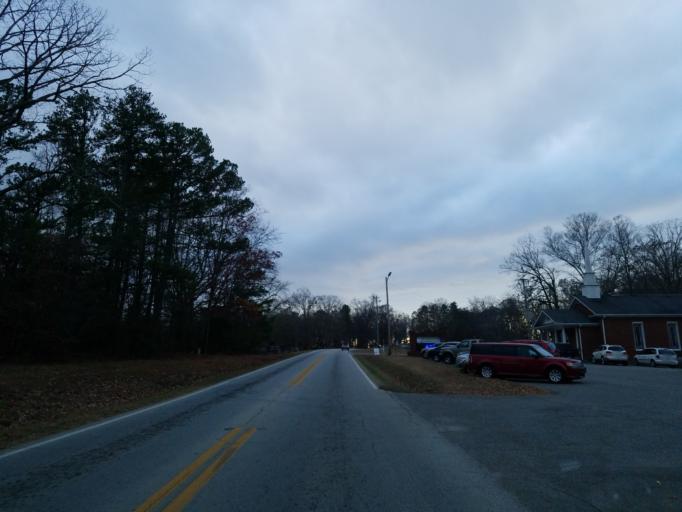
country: US
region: Georgia
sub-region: Dawson County
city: Dawsonville
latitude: 34.3667
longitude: -84.0416
